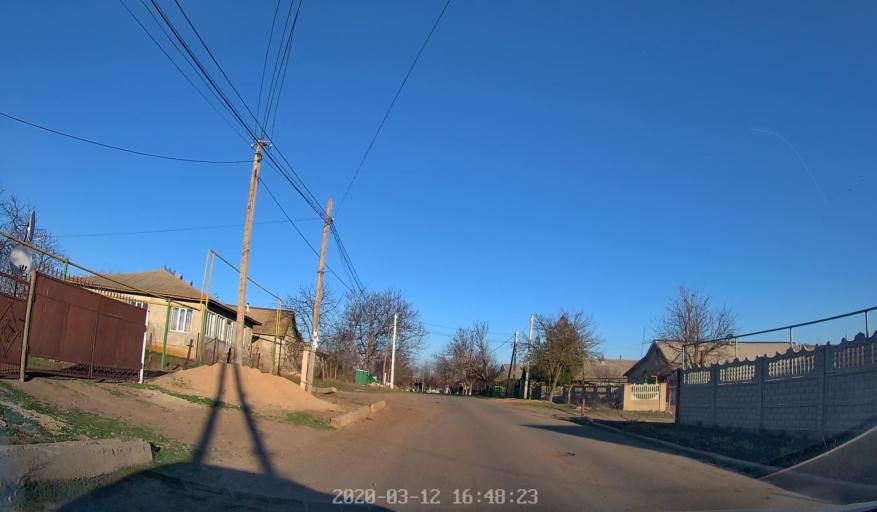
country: MD
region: Anenii Noi
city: Anenii Noi
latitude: 46.8135
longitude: 29.1931
